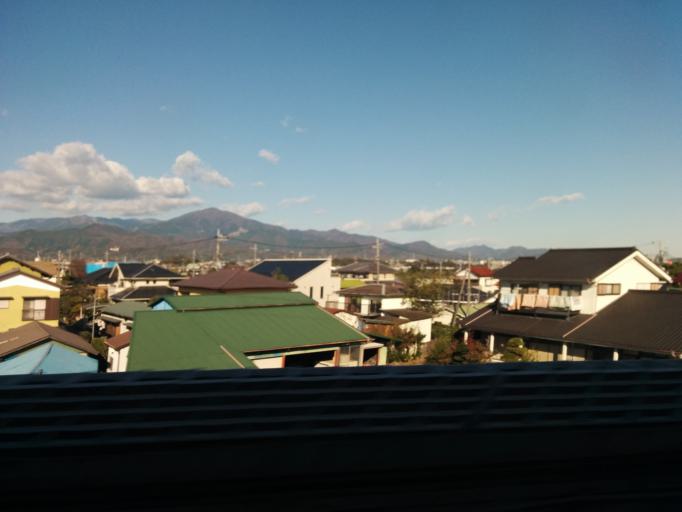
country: JP
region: Kanagawa
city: Isehara
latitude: 35.3592
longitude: 139.3252
